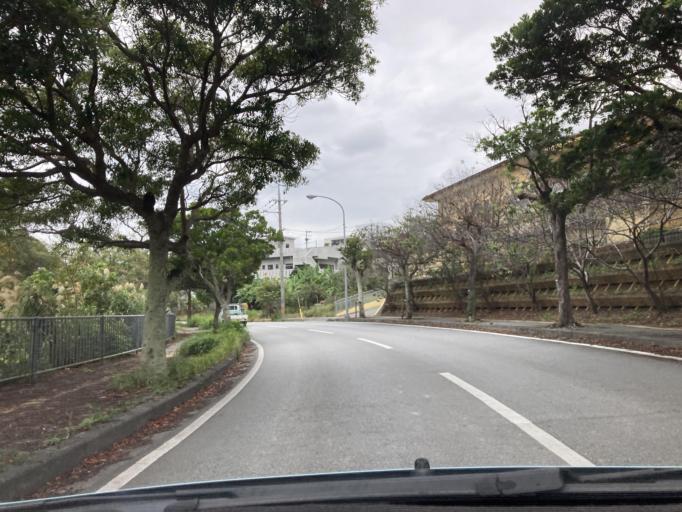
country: JP
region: Okinawa
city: Okinawa
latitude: 26.3440
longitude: 127.8088
